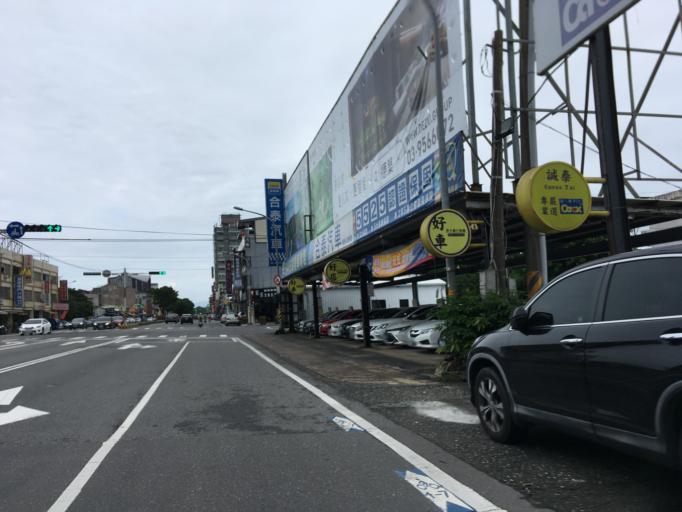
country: TW
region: Taiwan
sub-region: Yilan
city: Yilan
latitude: 24.7052
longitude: 121.7711
